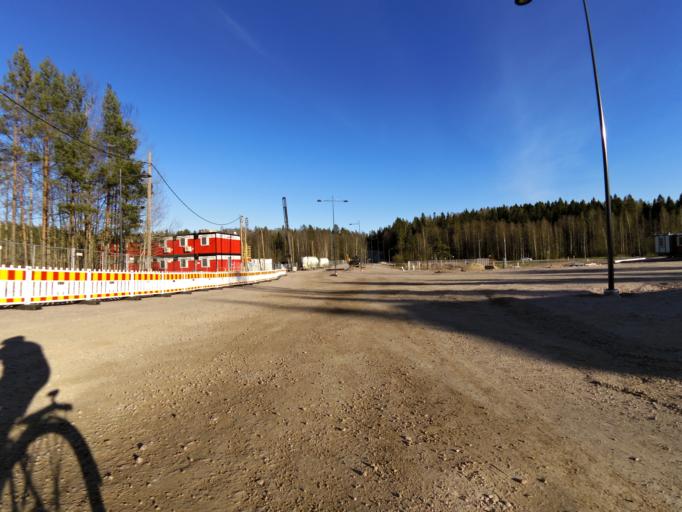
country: FI
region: Uusimaa
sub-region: Helsinki
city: Kauniainen
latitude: 60.1781
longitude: 24.7161
